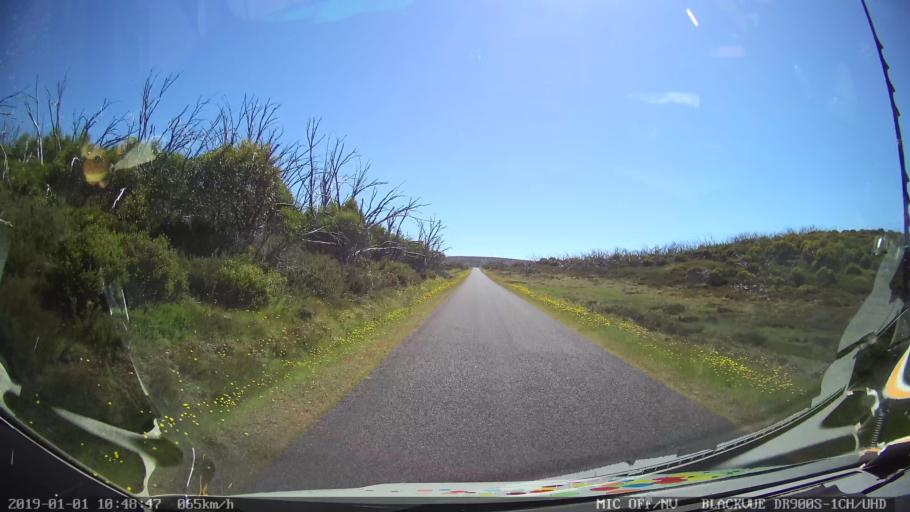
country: AU
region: New South Wales
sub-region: Snowy River
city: Jindabyne
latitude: -36.0379
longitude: 148.3639
